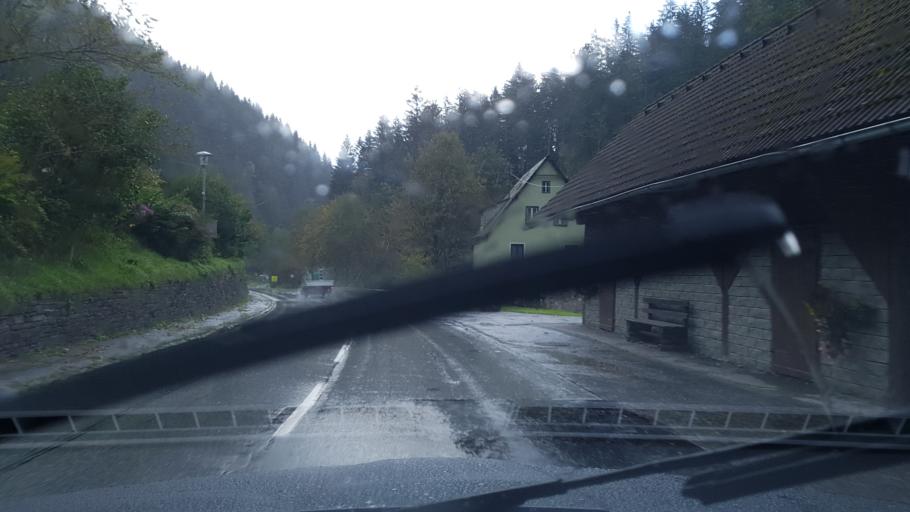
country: AT
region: Styria
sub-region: Politischer Bezirk Voitsberg
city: Salla
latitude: 47.1088
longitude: 14.9758
